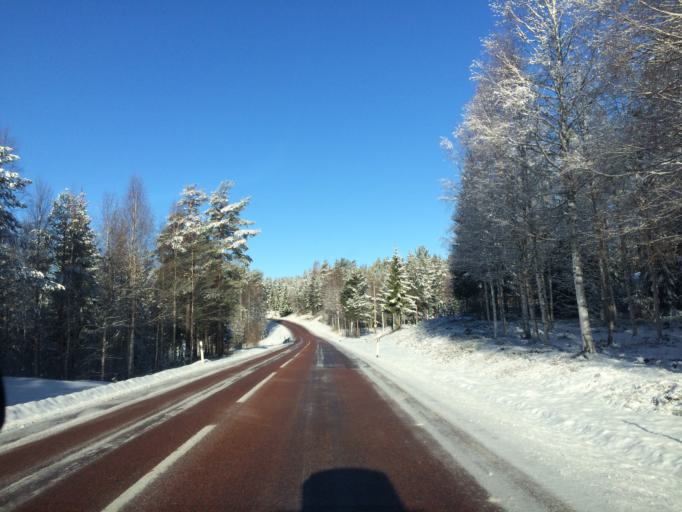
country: SE
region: Dalarna
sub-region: Mora Kommun
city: Mora
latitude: 60.8538
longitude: 14.2368
